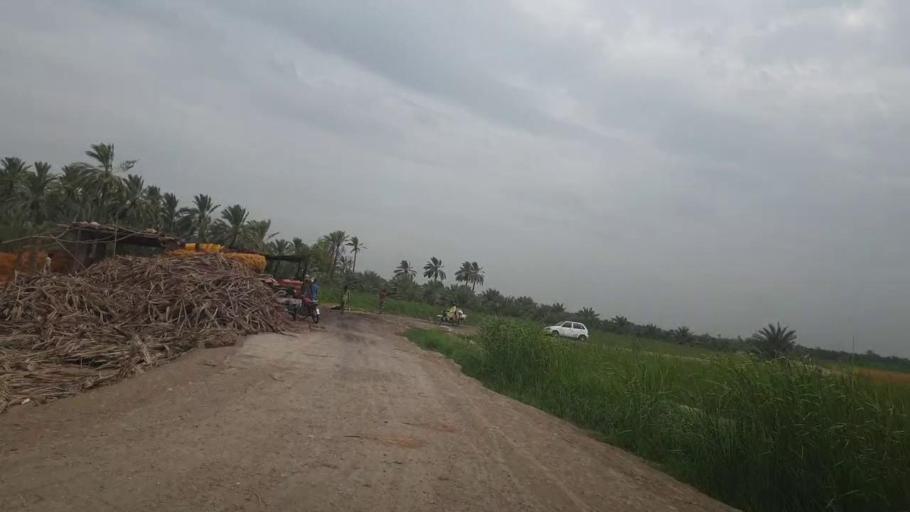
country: PK
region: Sindh
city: Khairpur
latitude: 27.5867
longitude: 68.7391
